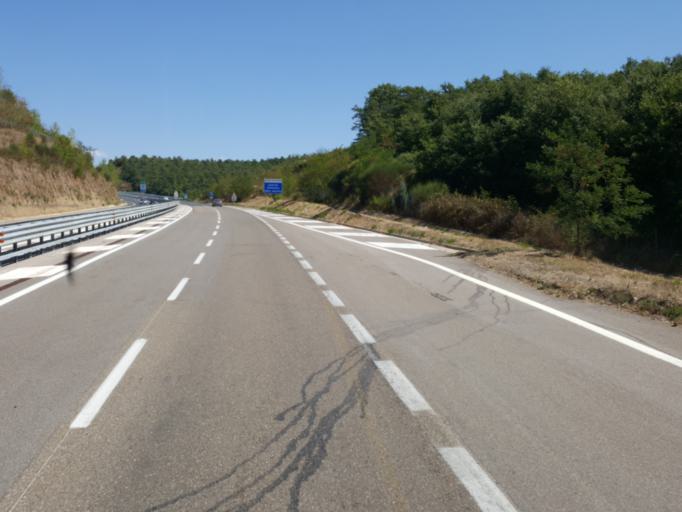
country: IT
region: Tuscany
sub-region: Provincia di Grosseto
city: Civitella Marittima
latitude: 42.9467
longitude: 11.2786
